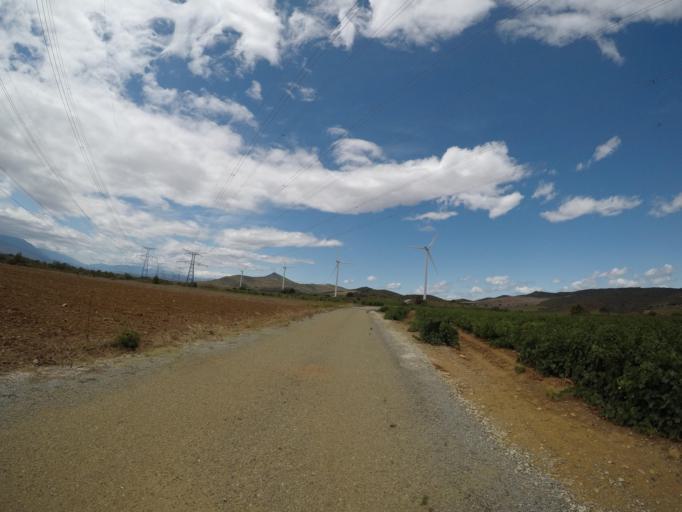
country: FR
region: Languedoc-Roussillon
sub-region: Departement des Pyrenees-Orientales
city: Pezilla-la-Riviere
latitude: 42.7215
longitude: 2.7546
